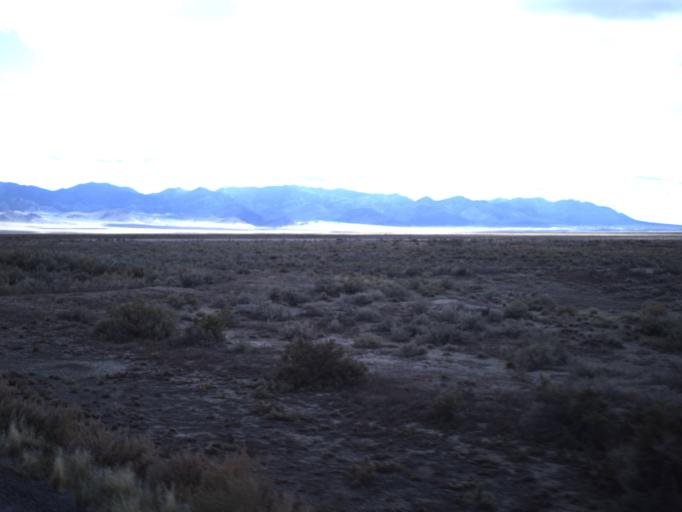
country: US
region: Utah
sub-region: Beaver County
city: Milford
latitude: 38.5434
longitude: -113.7119
